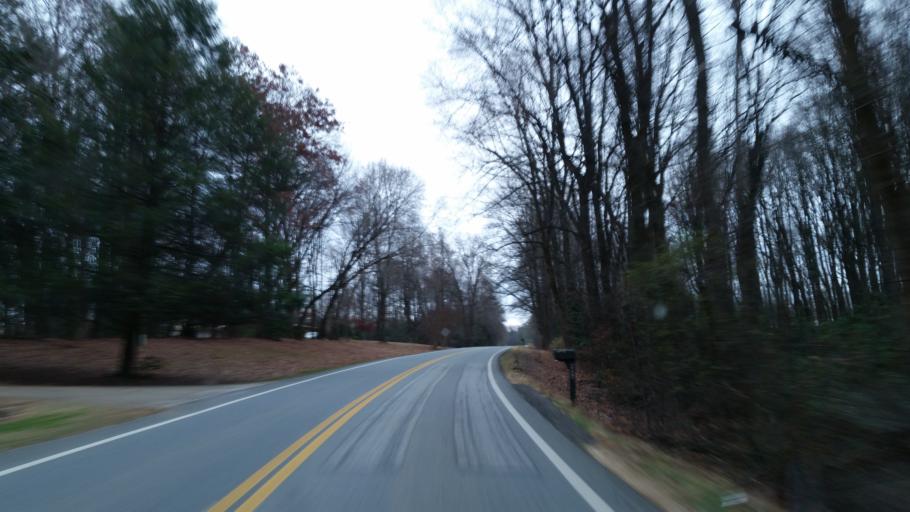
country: US
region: Georgia
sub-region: Dawson County
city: Dawsonville
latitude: 34.4949
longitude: -84.1886
